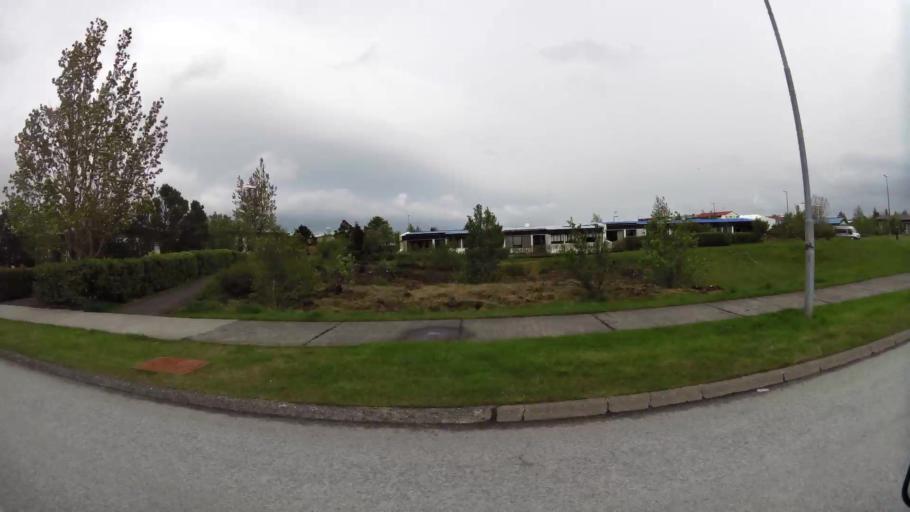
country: IS
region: Capital Region
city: Hafnarfjoerdur
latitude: 64.0780
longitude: -21.9672
